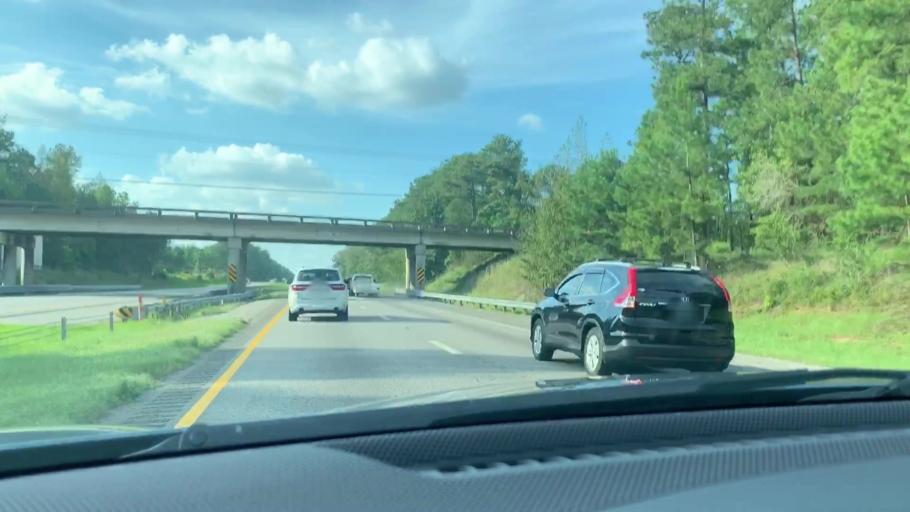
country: US
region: South Carolina
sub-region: Orangeburg County
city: Brookdale
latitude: 33.5335
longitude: -80.8032
